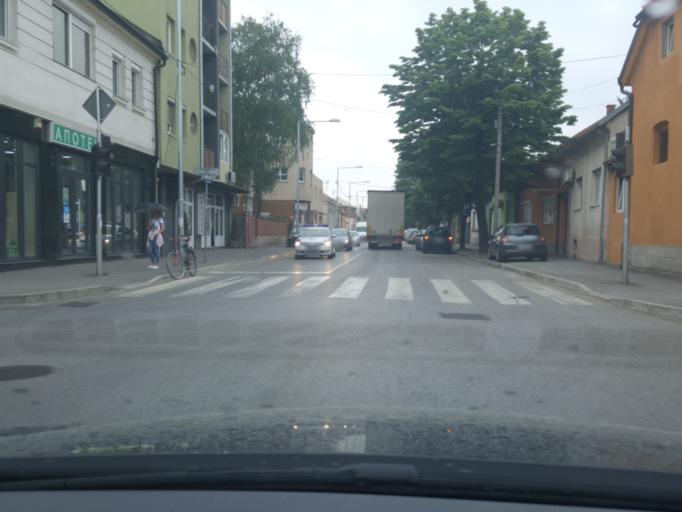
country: RS
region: Central Serbia
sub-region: Kolubarski Okrug
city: Valjevo
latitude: 44.2719
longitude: 19.8801
